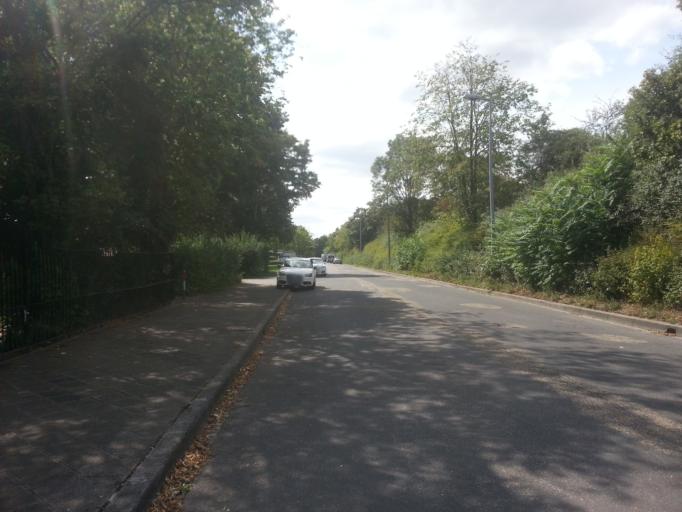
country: DE
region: Hesse
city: Viernheim
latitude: 49.5161
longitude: 8.5408
